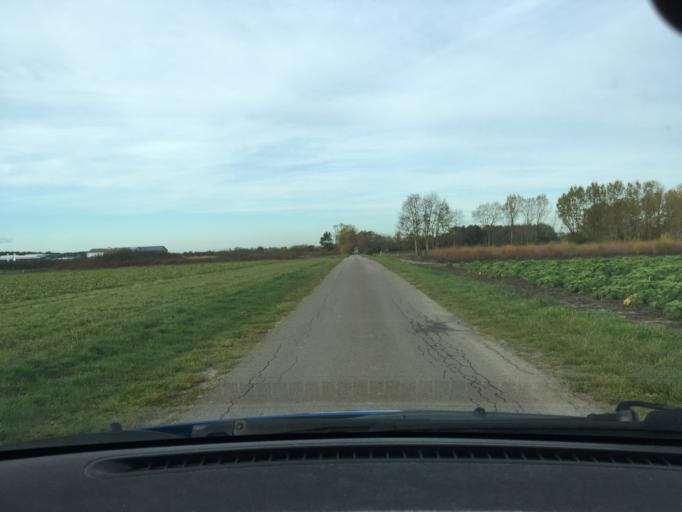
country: DE
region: Lower Saxony
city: Wittorf
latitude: 53.3130
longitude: 10.3774
